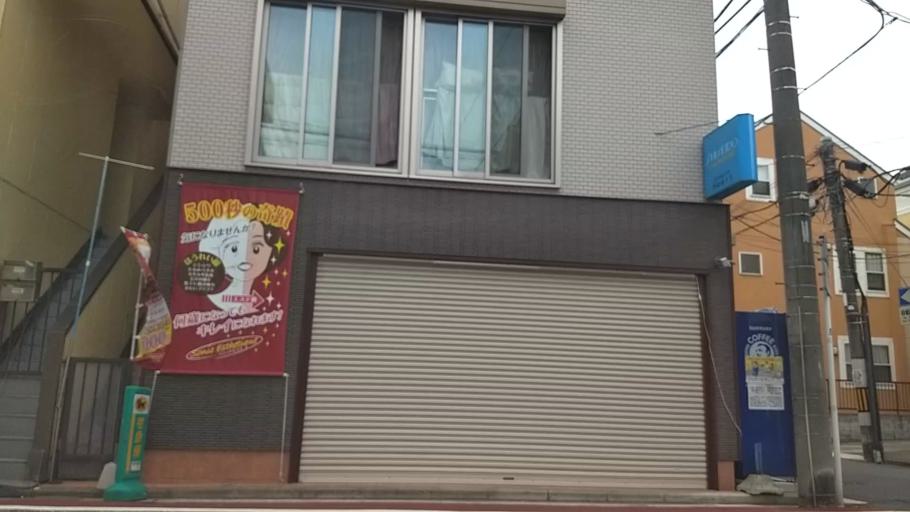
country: JP
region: Kanagawa
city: Yokohama
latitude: 35.4393
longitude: 139.6154
